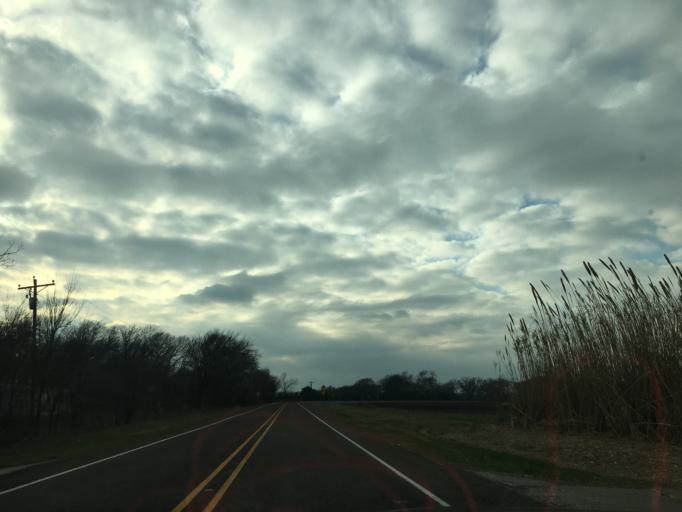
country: US
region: Texas
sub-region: Ellis County
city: Palmer
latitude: 32.4478
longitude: -96.7163
